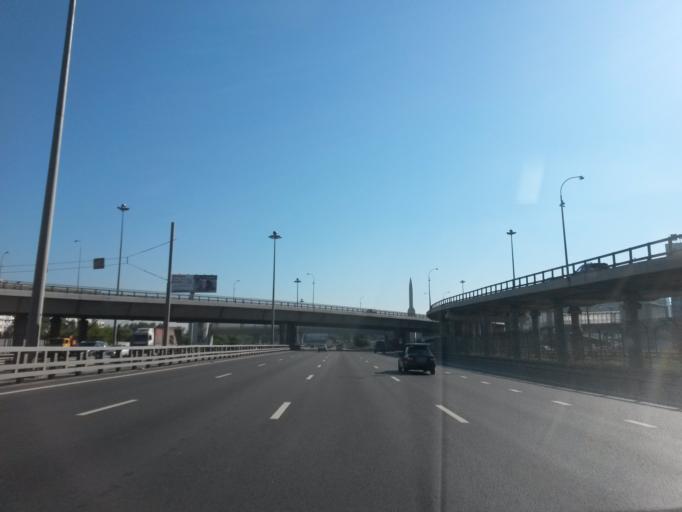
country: RU
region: Moskovskaya
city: Korolev
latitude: 55.9135
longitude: 37.7862
